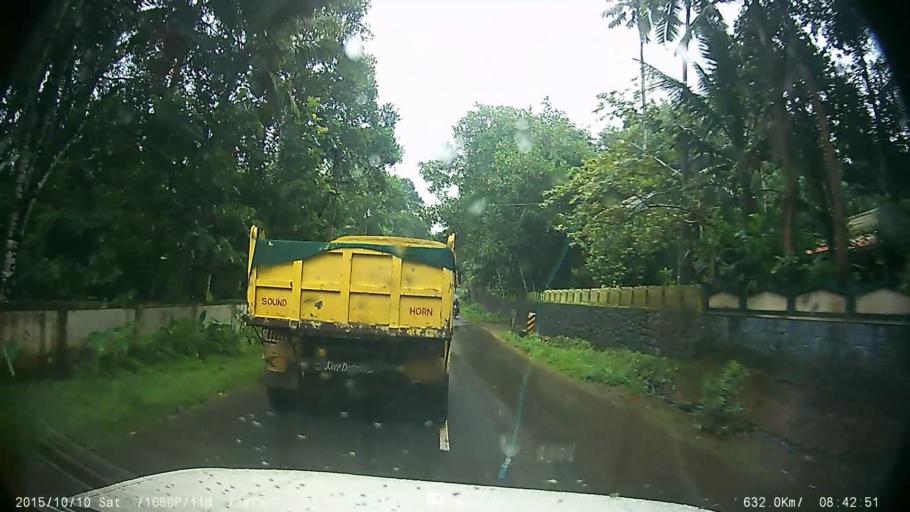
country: IN
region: Kerala
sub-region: Kottayam
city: Palackattumala
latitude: 9.7492
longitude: 76.5386
